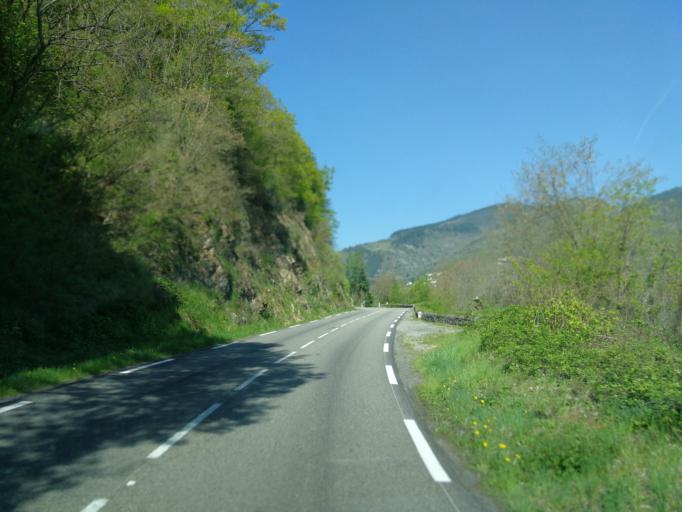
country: FR
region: Rhone-Alpes
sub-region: Departement de l'Ardeche
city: Le Cheylard
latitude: 44.9089
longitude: 4.4530
